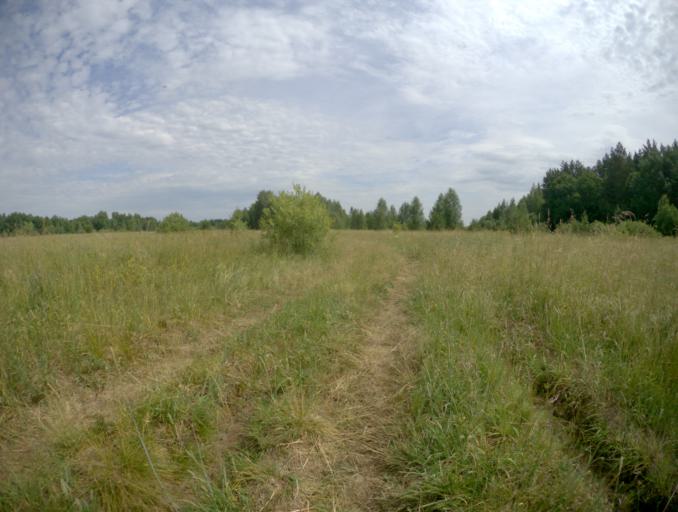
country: RU
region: Vladimir
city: Raduzhnyy
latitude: 56.0294
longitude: 40.2518
